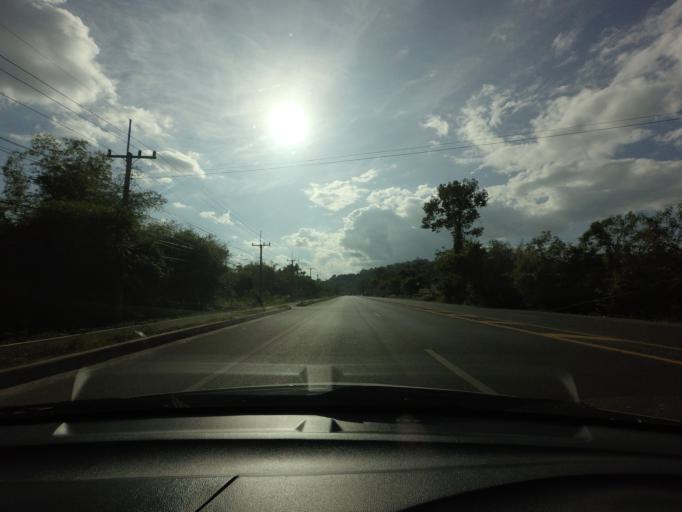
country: TH
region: Nakhon Nayok
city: Nakhon Nayok
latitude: 14.2885
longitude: 101.2807
